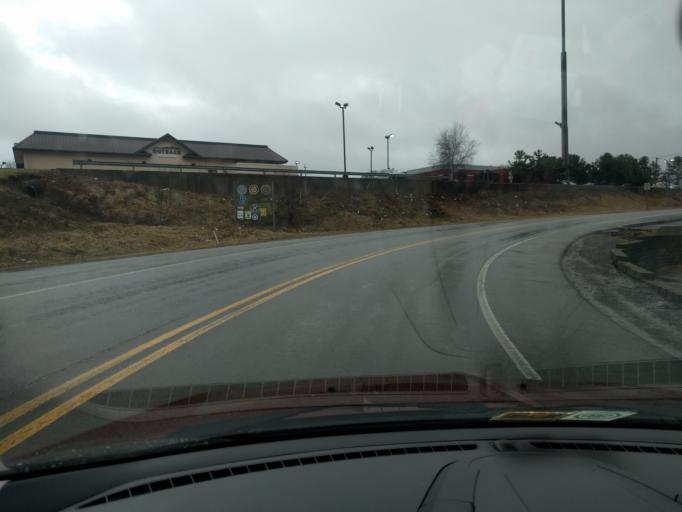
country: US
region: West Virginia
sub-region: Raleigh County
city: Mabscott
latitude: 37.7927
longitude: -81.2139
